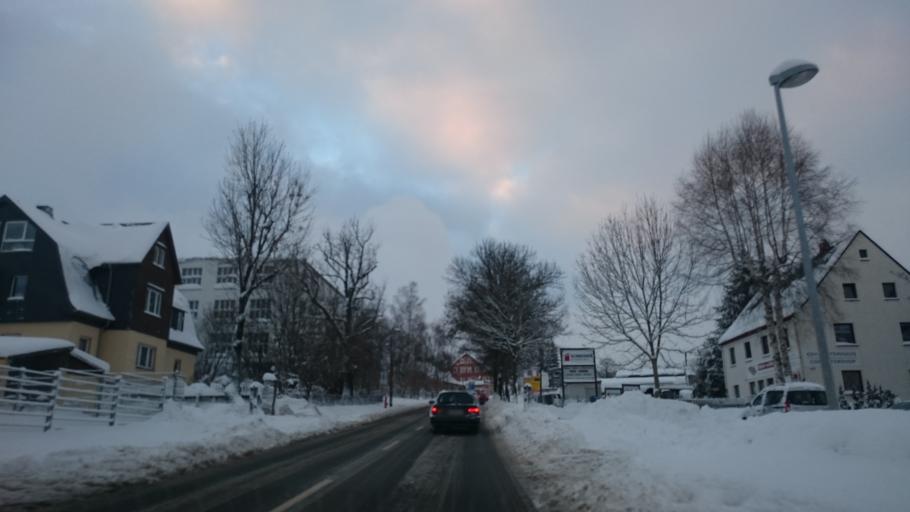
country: DE
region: Saxony
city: Zwonitz
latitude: 50.6330
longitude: 12.7973
